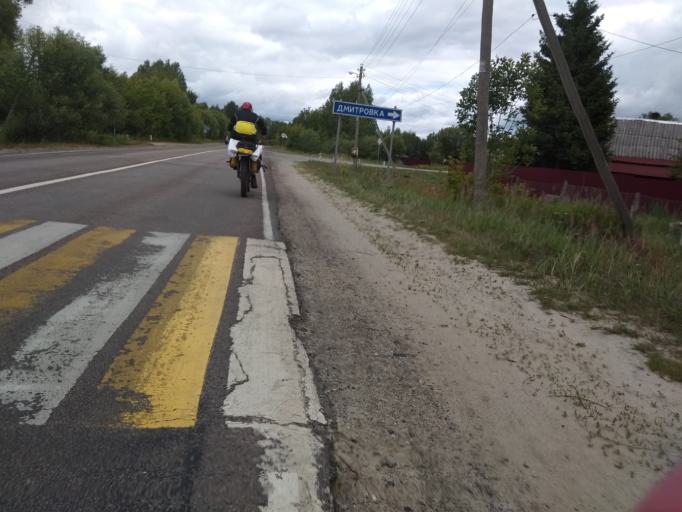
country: RU
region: Moskovskaya
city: Misheronskiy
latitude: 55.6021
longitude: 39.7068
